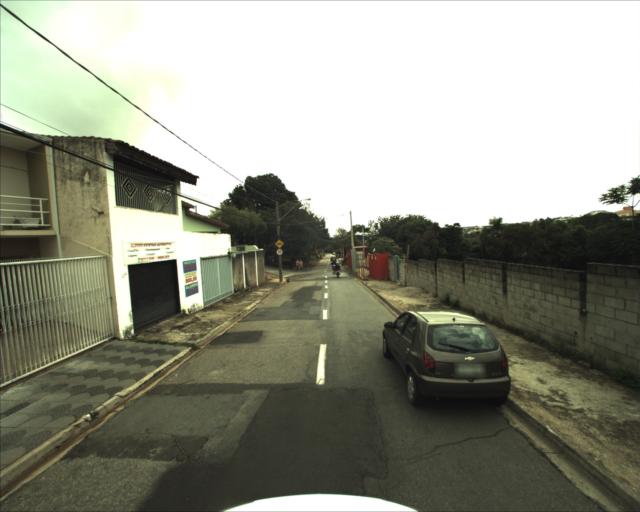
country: BR
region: Sao Paulo
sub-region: Sorocaba
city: Sorocaba
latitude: -23.5036
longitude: -47.4921
